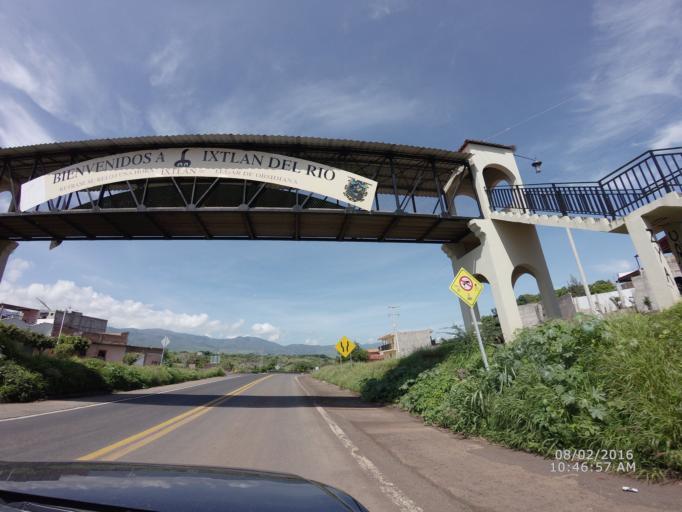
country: MX
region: Nayarit
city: Ixtlan del Rio
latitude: 21.0302
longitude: -104.3534
